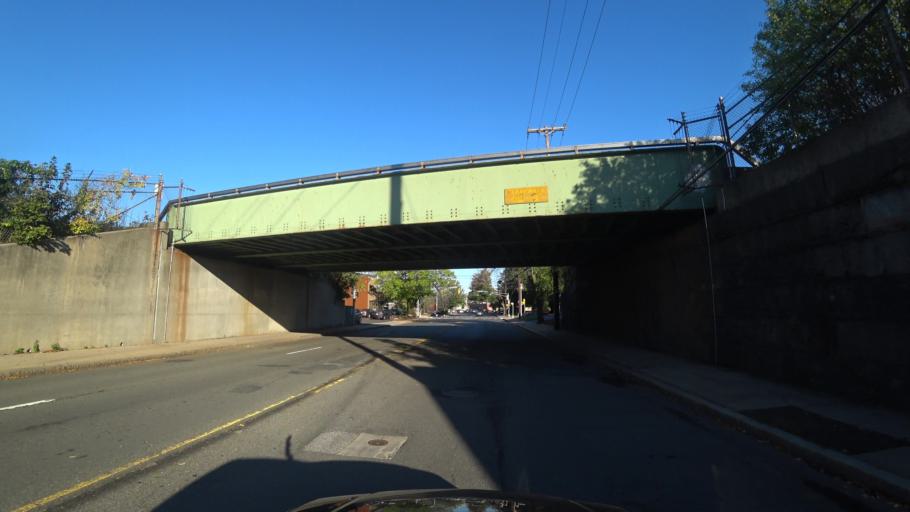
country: US
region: Massachusetts
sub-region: Middlesex County
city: Malden
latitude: 42.4233
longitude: -71.0760
